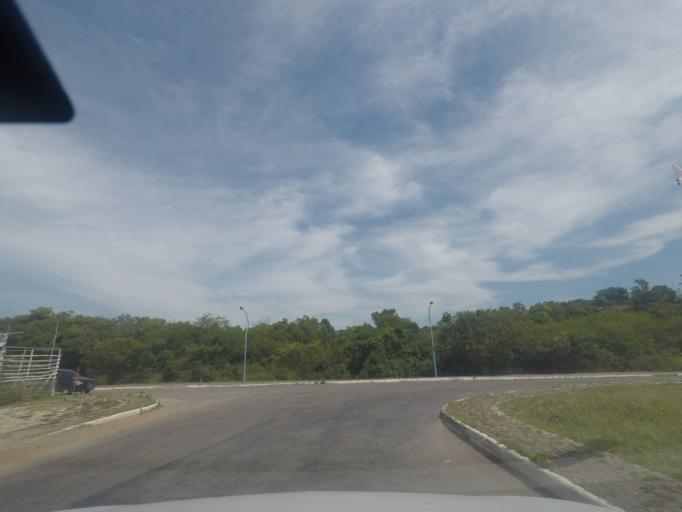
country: BR
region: Rio de Janeiro
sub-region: Marica
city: Marica
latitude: -22.9463
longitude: -42.7529
